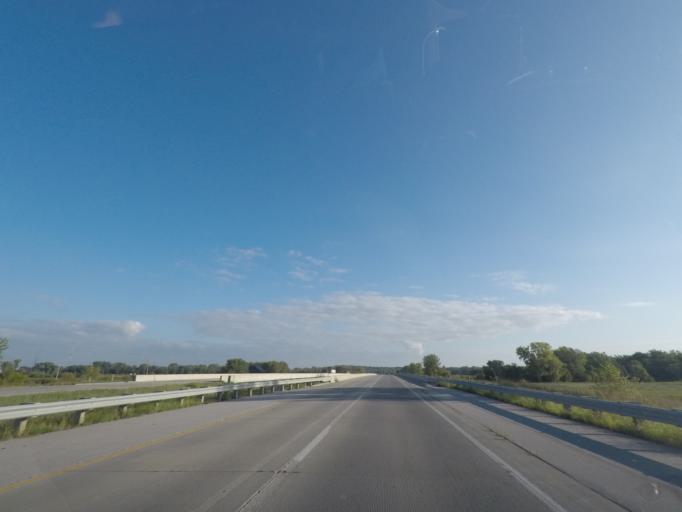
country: US
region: Iowa
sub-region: Polk County
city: Pleasant Hill
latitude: 41.5445
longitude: -93.5147
